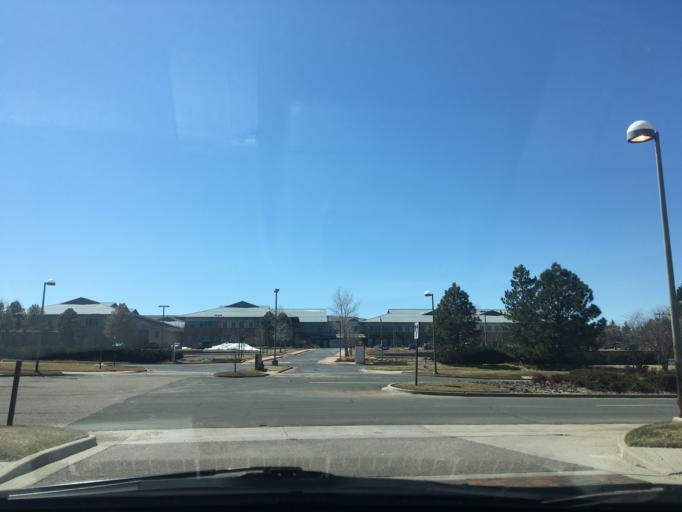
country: US
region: Colorado
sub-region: Broomfield County
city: Broomfield
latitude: 39.9221
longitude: -105.1267
